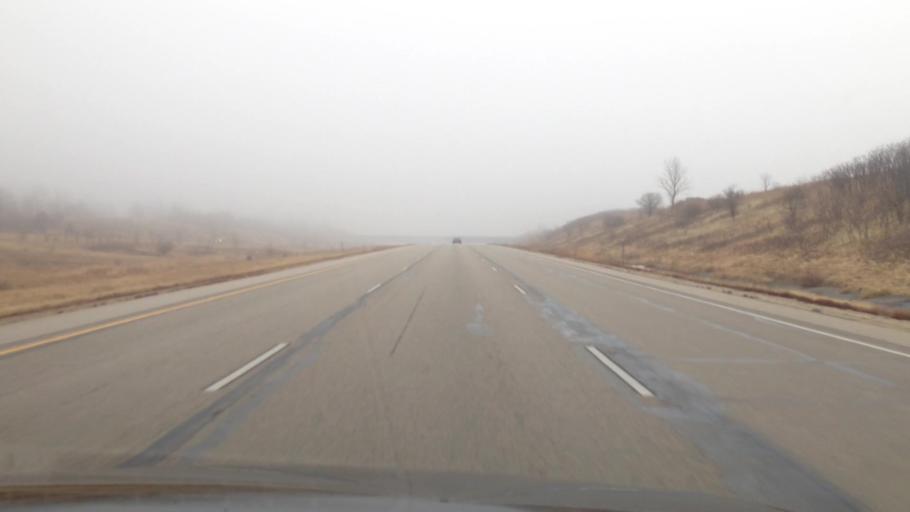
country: US
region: Wisconsin
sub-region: Walworth County
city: East Troy
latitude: 42.7376
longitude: -88.4546
